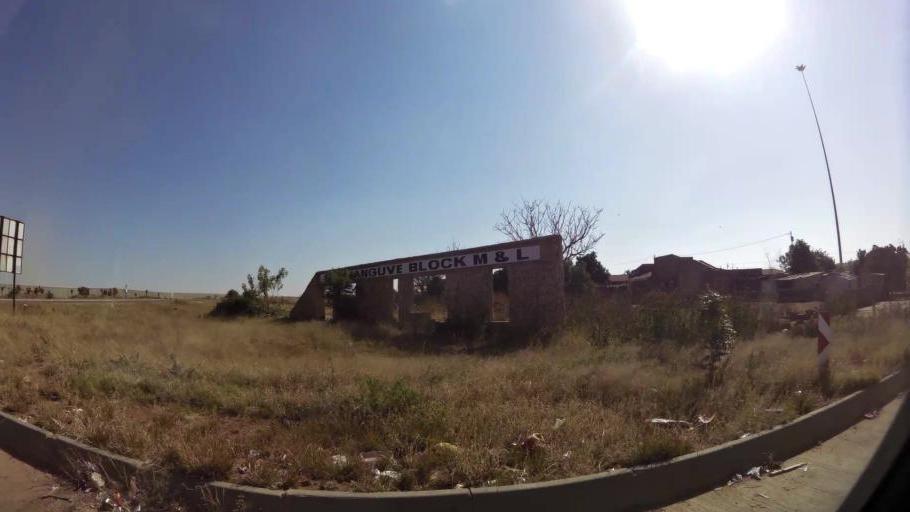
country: ZA
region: Gauteng
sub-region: City of Tshwane Metropolitan Municipality
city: Mabopane
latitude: -25.5549
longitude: 28.1012
